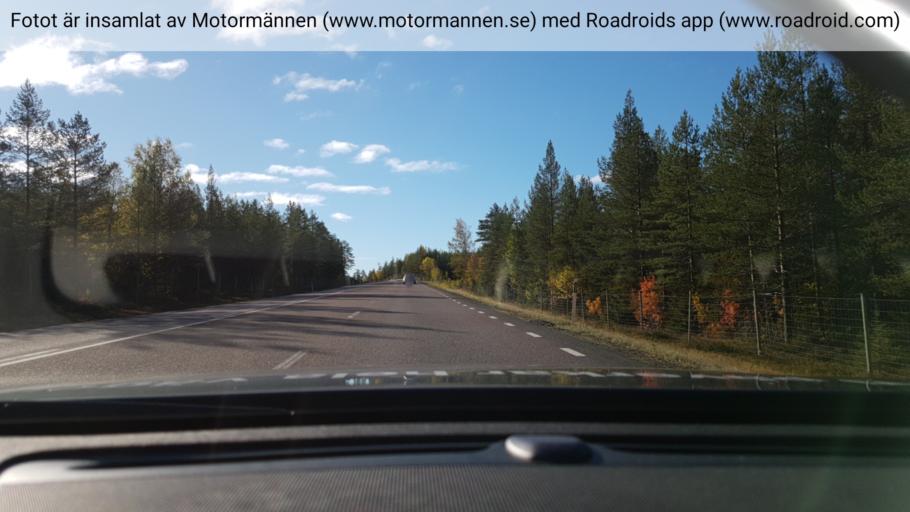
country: SE
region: Vaesterbotten
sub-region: Skelleftea Kommun
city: Burea
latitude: 64.4406
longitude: 21.2823
